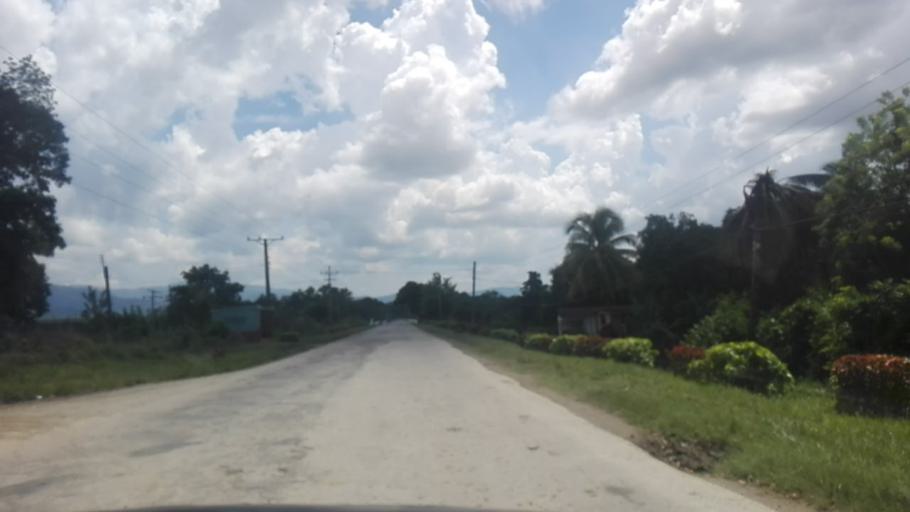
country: CU
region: Granma
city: Bartolome Maso
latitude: 20.1487
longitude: -76.9597
